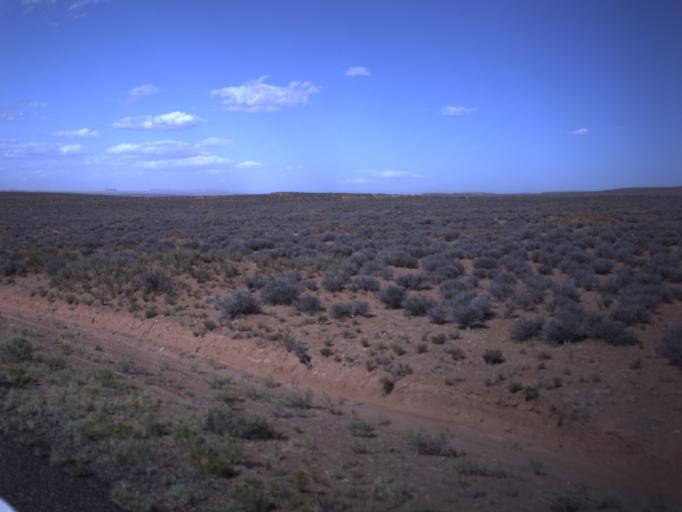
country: US
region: Utah
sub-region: Wayne County
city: Loa
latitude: 38.1558
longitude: -110.6211
